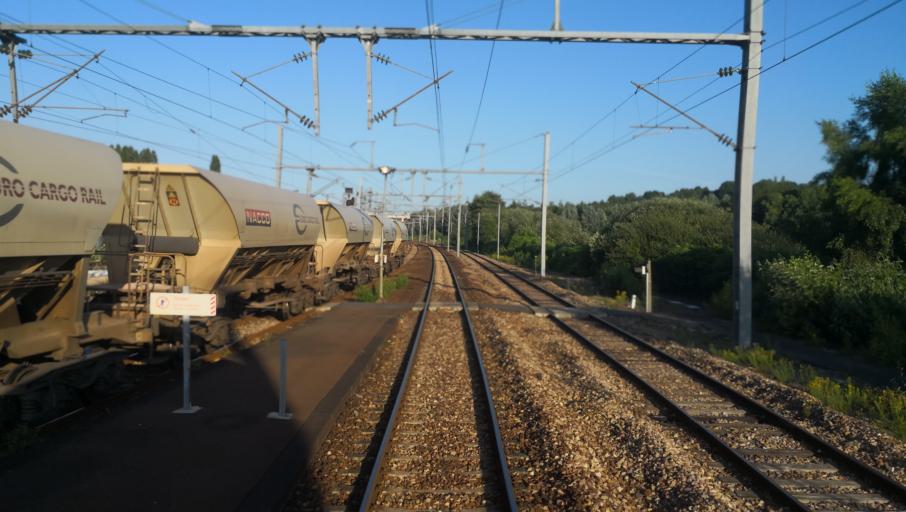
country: FR
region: Lower Normandy
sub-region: Departement du Calvados
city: Lisieux
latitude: 49.1364
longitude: 0.2337
